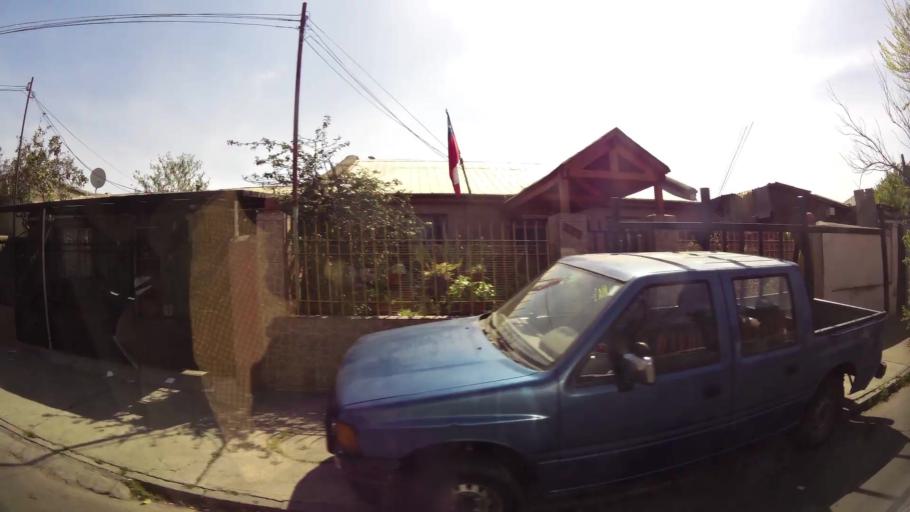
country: CL
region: Santiago Metropolitan
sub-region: Provincia de Maipo
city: San Bernardo
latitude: -33.5363
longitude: -70.6756
